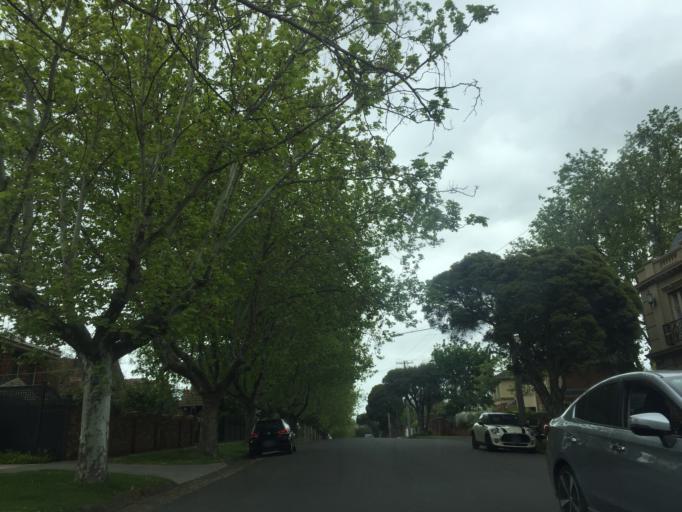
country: AU
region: Victoria
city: Balwyn
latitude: -37.8107
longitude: 145.0559
